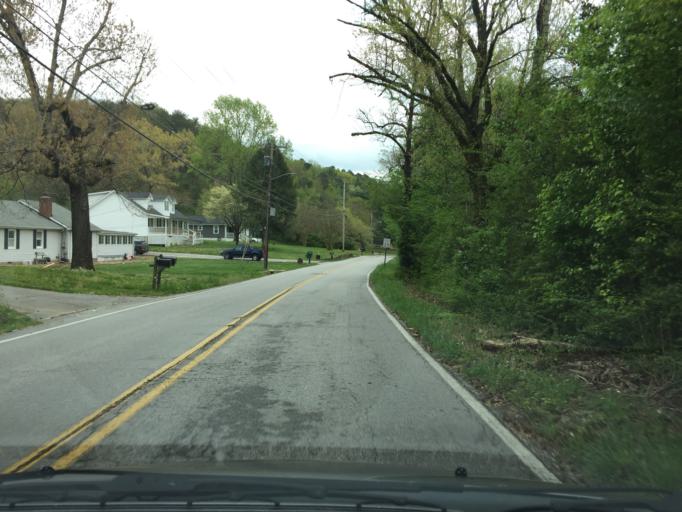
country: US
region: Tennessee
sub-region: Hamilton County
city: Falling Water
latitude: 35.1569
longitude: -85.2464
